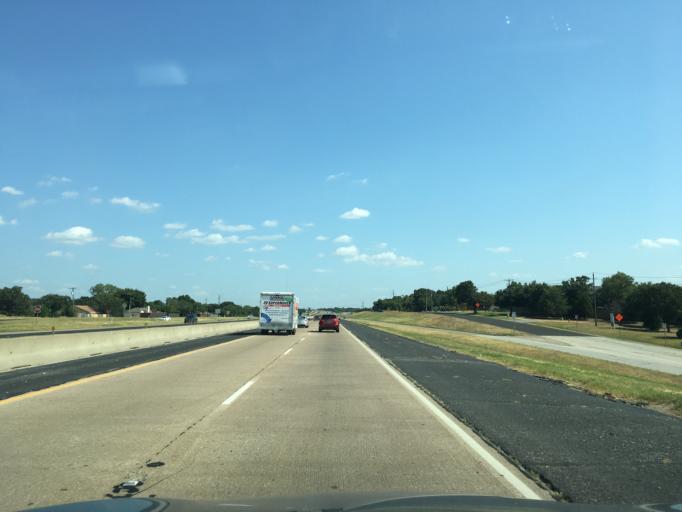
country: US
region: Texas
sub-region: Tarrant County
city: Kennedale
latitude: 32.6451
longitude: -97.1846
